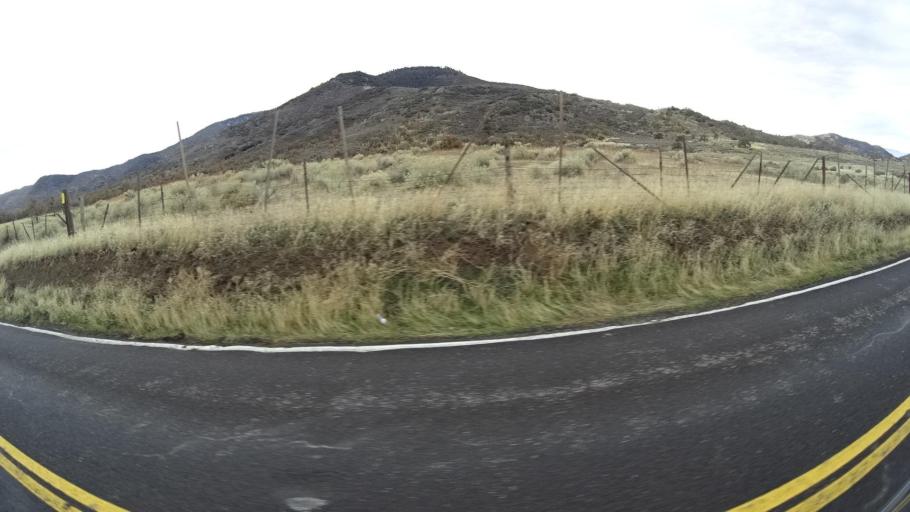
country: US
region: California
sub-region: Kern County
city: Stallion Springs
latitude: 35.0948
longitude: -118.5863
